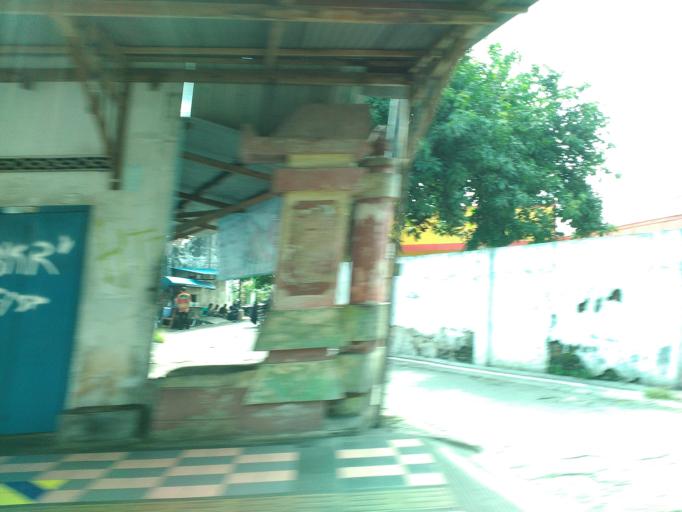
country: ID
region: Central Java
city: Klaten
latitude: -7.6944
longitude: 110.6103
